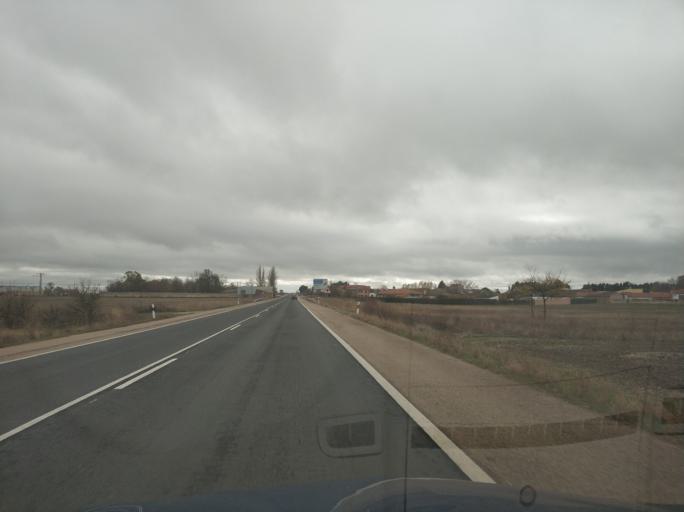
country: ES
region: Castille and Leon
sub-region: Provincia de Salamanca
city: Pedrosillo el Ralo
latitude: 41.0625
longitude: -5.5452
